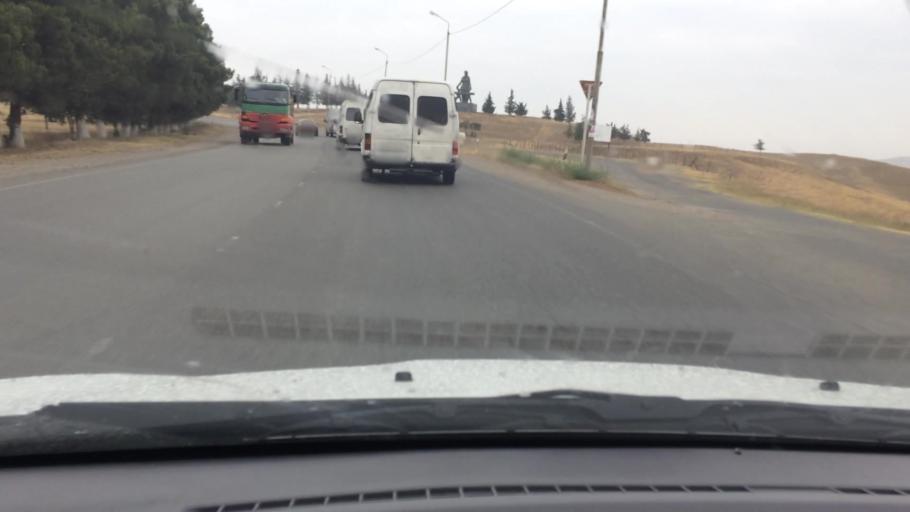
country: GE
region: Kvemo Kartli
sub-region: Marneuli
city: Marneuli
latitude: 41.4999
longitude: 44.8034
